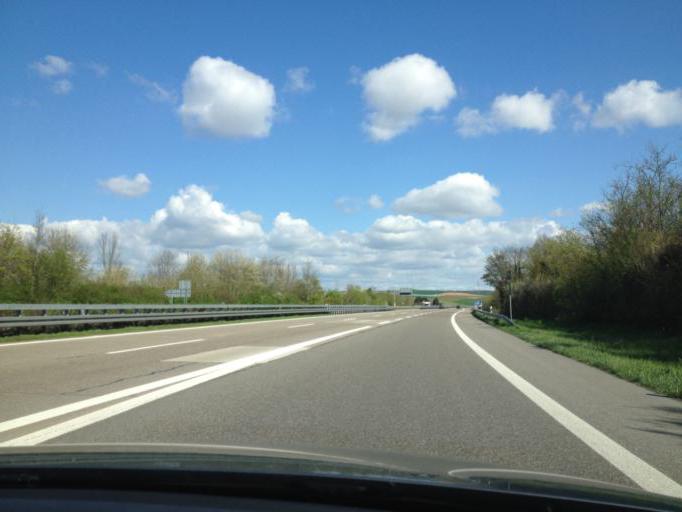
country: DE
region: Baden-Wuerttemberg
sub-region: Regierungsbezirk Stuttgart
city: Neuenstadt am Kocher
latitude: 49.2353
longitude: 9.3492
